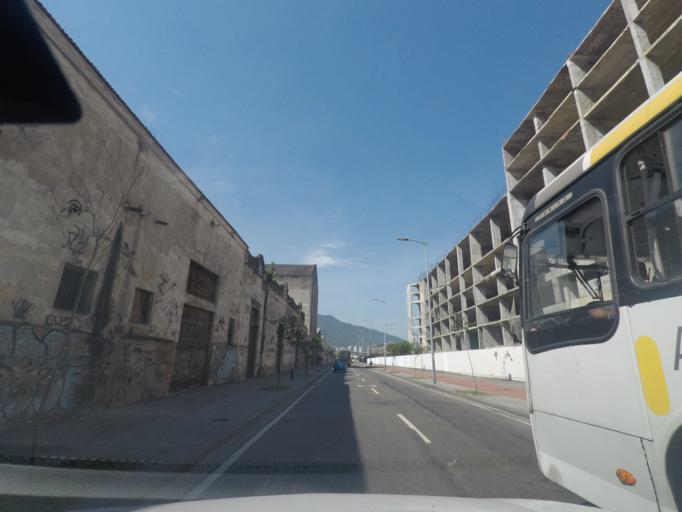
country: BR
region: Rio de Janeiro
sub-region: Rio De Janeiro
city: Rio de Janeiro
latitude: -22.9038
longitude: -43.2068
